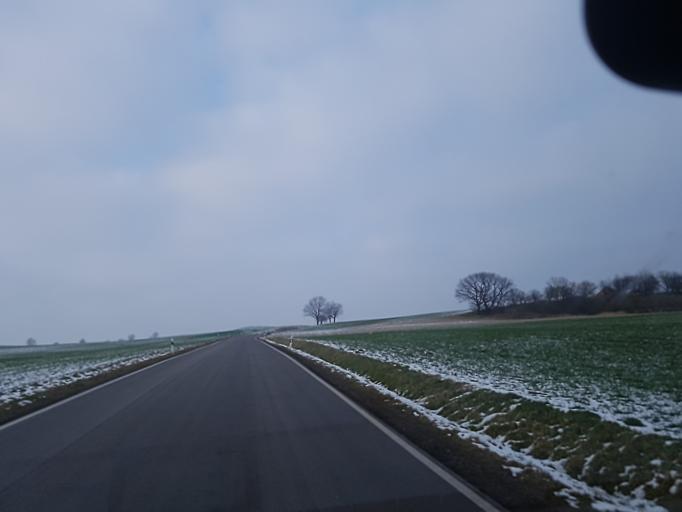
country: DE
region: Saxony
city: Cavertitz
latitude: 51.3500
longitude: 13.1391
